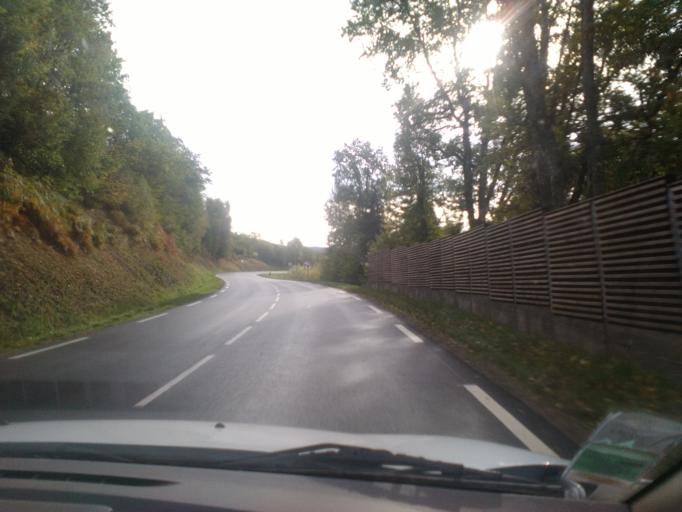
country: FR
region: Lorraine
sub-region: Departement des Vosges
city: Corcieux
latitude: 48.1659
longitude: 6.8960
